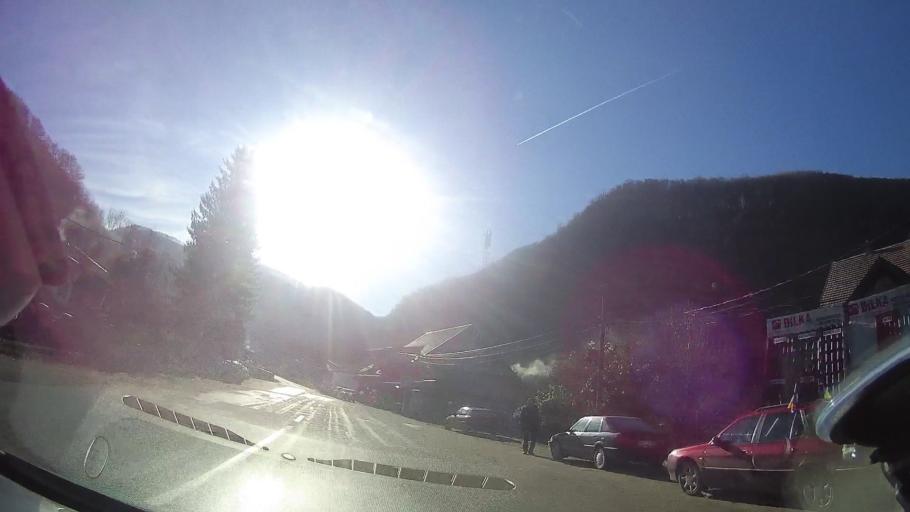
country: RO
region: Bihor
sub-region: Comuna Bulz
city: Bulz
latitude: 46.9231
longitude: 22.6538
